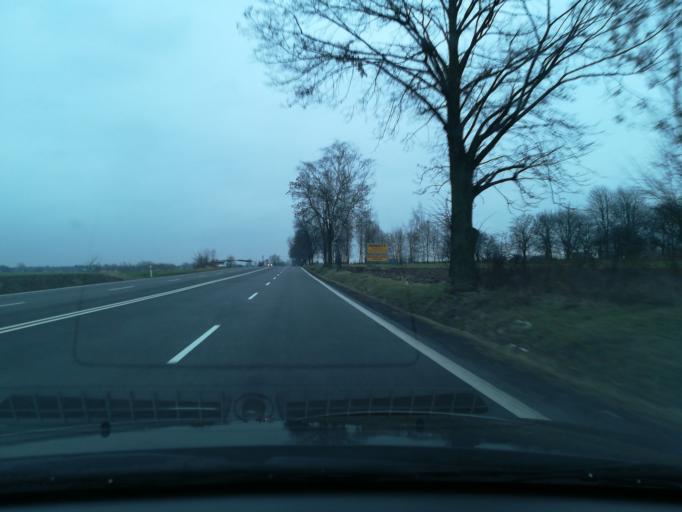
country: PL
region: Subcarpathian Voivodeship
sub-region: Powiat lancucki
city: Kosina
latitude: 50.0749
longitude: 22.3086
